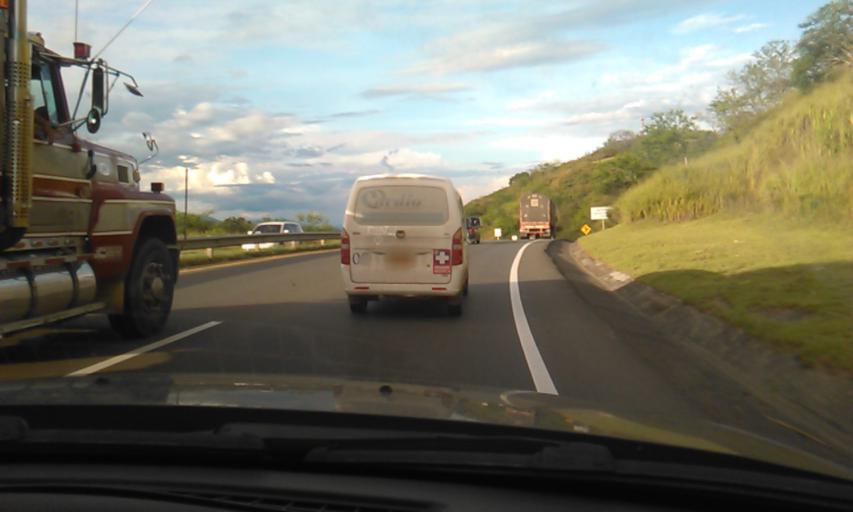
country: CO
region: Valle del Cauca
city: Bugalagrande
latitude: 4.2059
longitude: -76.1539
